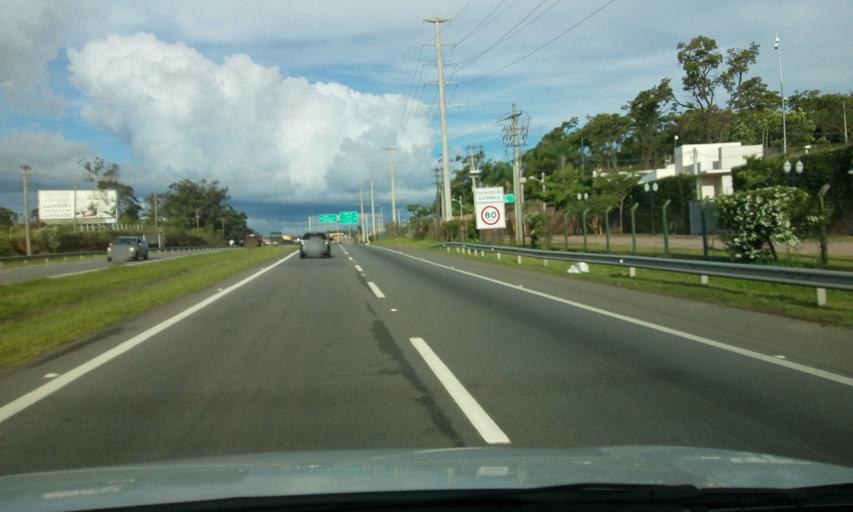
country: BR
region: Sao Paulo
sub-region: Jundiai
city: Jundiai
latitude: -23.1548
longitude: -46.8840
